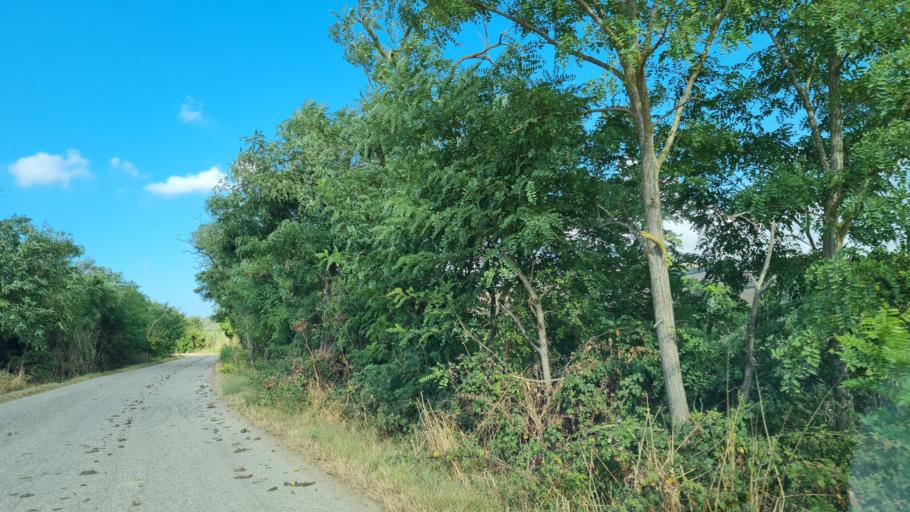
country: IT
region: Latium
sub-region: Provincia di Viterbo
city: Tarquinia
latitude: 42.2607
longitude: 11.7629
